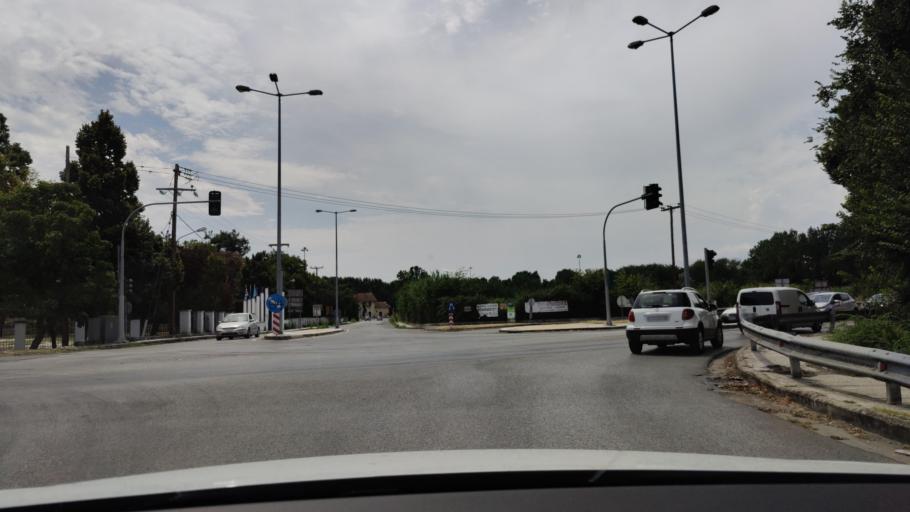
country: GR
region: Central Macedonia
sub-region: Nomos Serron
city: Serres
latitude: 41.0761
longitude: 23.5379
